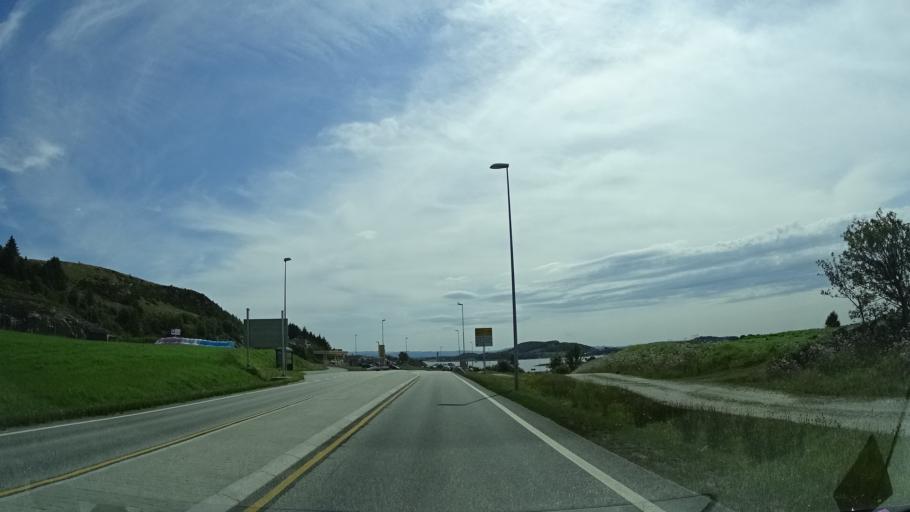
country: NO
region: Rogaland
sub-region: Rennesoy
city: Vikevag
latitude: 59.0655
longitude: 5.6748
